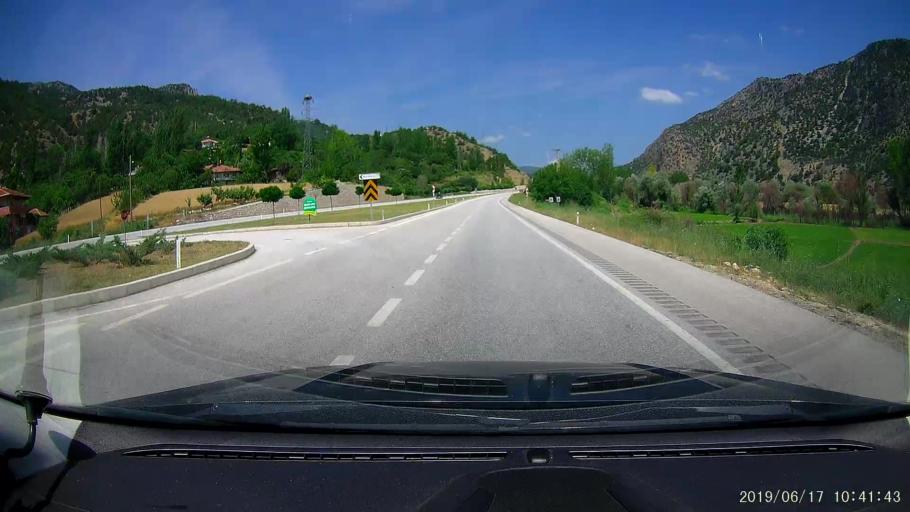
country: TR
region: Corum
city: Kargi
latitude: 41.0423
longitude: 34.5699
